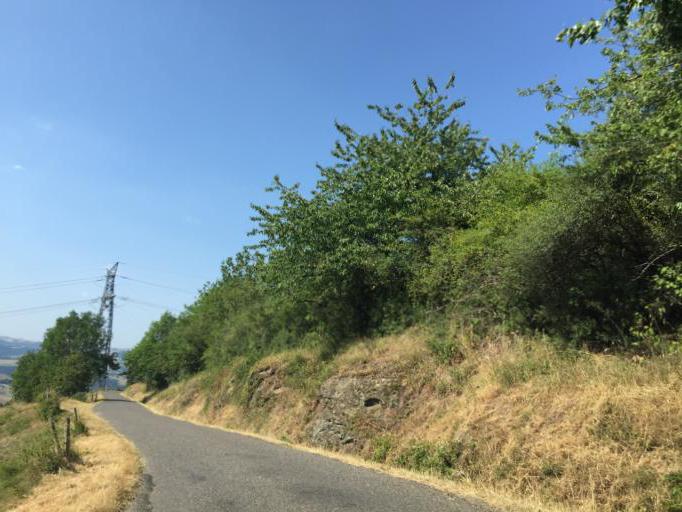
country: FR
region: Rhone-Alpes
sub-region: Departement de la Loire
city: Saint-Jean-Bonnefonds
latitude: 45.4383
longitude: 4.4878
